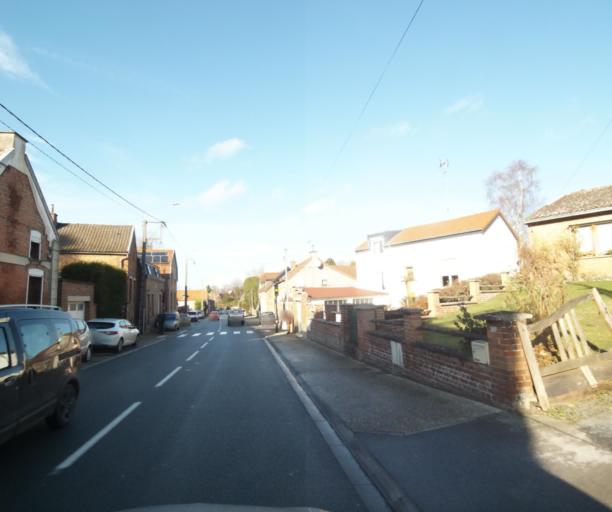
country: FR
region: Nord-Pas-de-Calais
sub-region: Departement du Nord
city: Preseau
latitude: 50.3091
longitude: 3.5799
